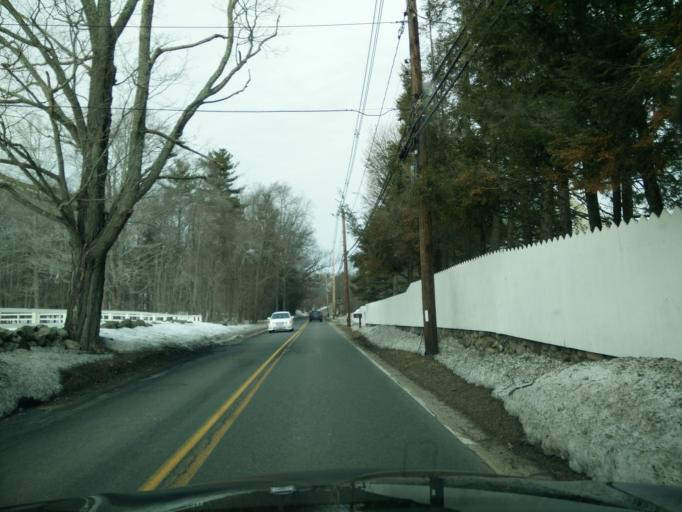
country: US
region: Massachusetts
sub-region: Norfolk County
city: Westwood
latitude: 42.1900
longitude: -71.2485
